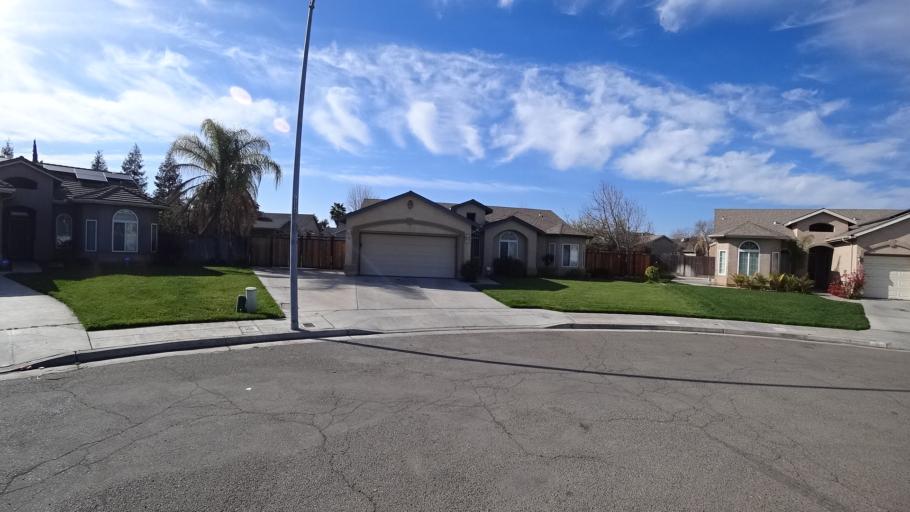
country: US
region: California
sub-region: Fresno County
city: West Park
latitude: 36.8020
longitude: -119.8968
